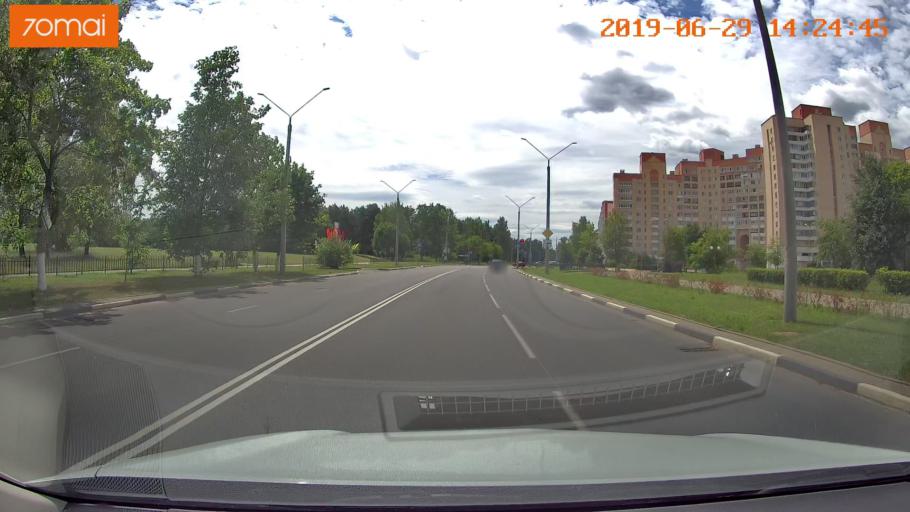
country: BY
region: Minsk
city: Salihorsk
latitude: 52.7798
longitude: 27.5468
